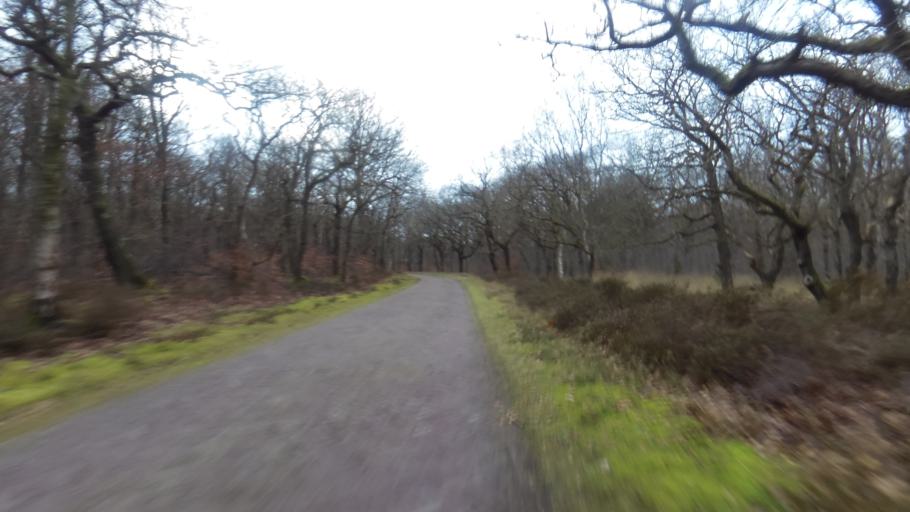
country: NL
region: North Holland
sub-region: Gemeente Bergen
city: Egmond aan Zee
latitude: 52.6771
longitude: 4.6724
